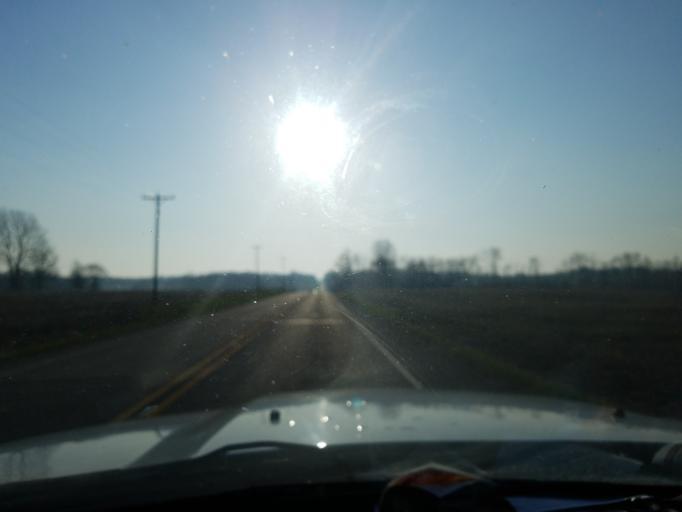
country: US
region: Indiana
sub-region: Vigo County
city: Seelyville
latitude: 39.3901
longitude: -87.2377
